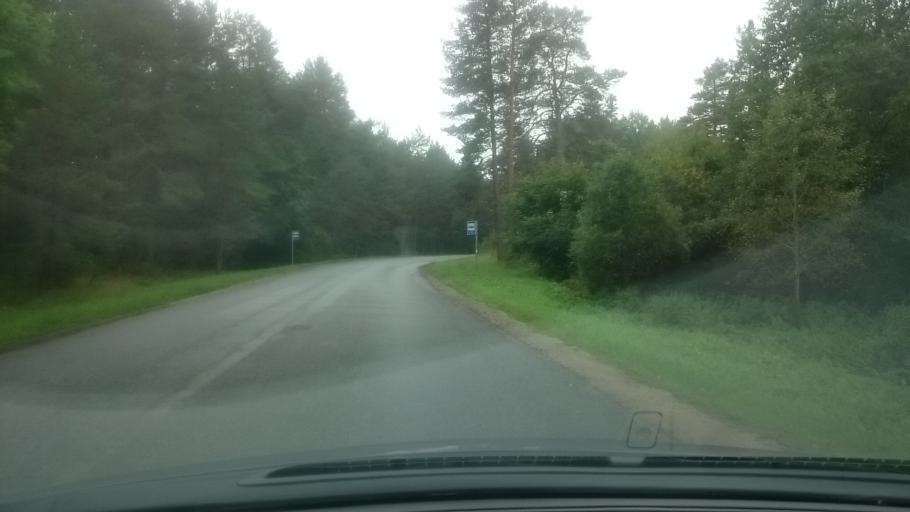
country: EE
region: Harju
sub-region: Raasiku vald
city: Raasiku
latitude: 59.4643
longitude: 25.2392
